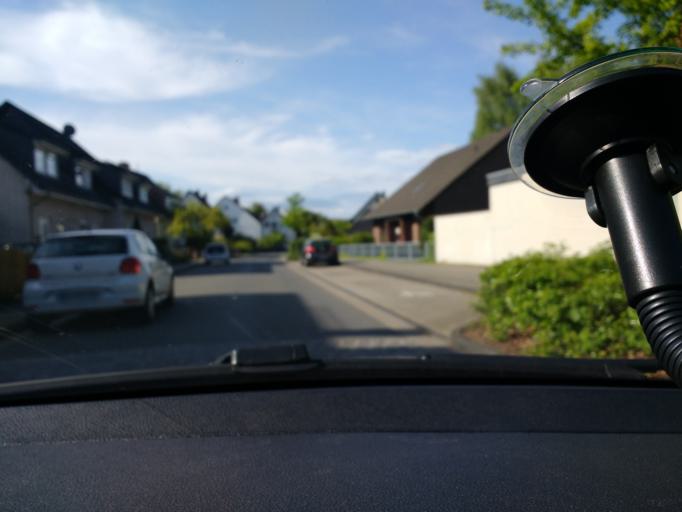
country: DE
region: Lower Saxony
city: Gifhorn
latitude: 52.4813
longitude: 10.5407
